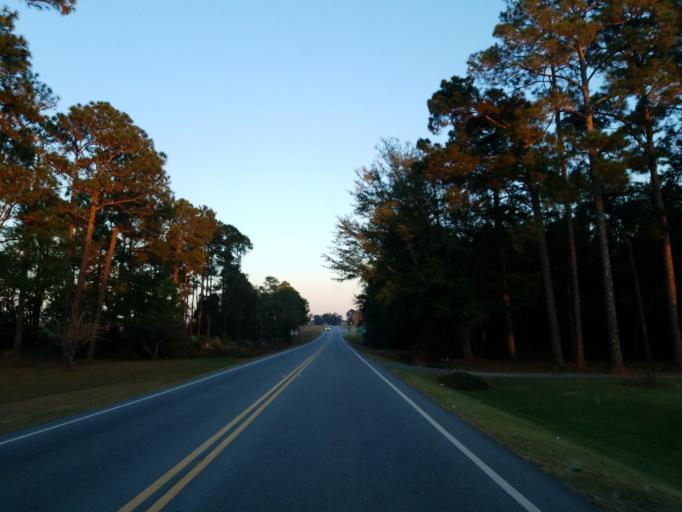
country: US
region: Georgia
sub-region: Irwin County
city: Ocilla
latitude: 31.6459
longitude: -83.3548
